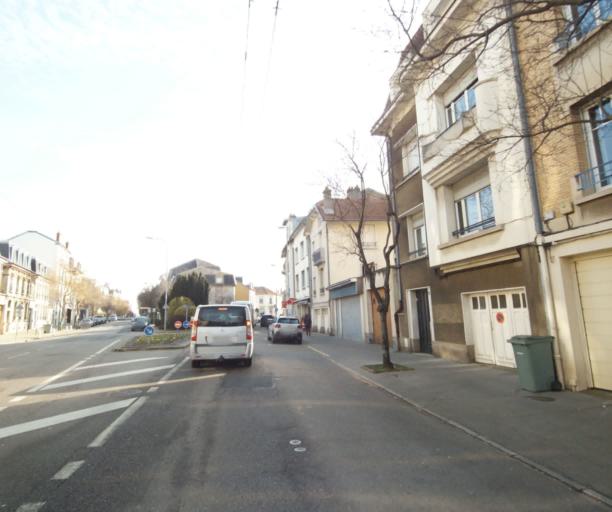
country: FR
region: Lorraine
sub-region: Departement de Meurthe-et-Moselle
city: Laxou
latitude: 48.6847
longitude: 6.1544
